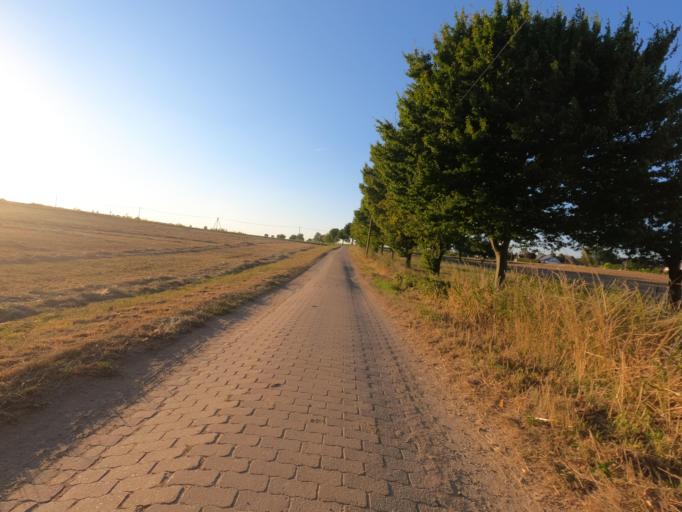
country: DE
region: North Rhine-Westphalia
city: Julich
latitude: 50.9802
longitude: 6.3607
